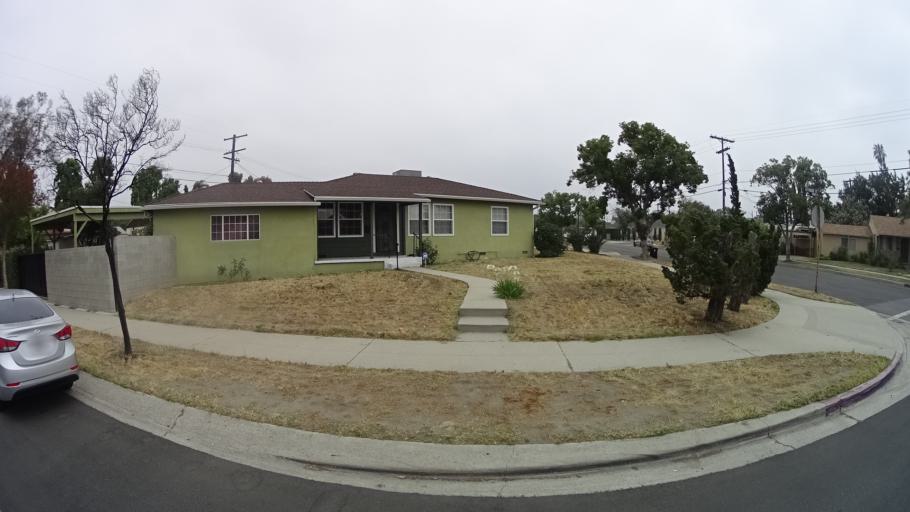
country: US
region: California
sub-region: Los Angeles County
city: Van Nuys
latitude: 34.1904
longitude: -118.4121
